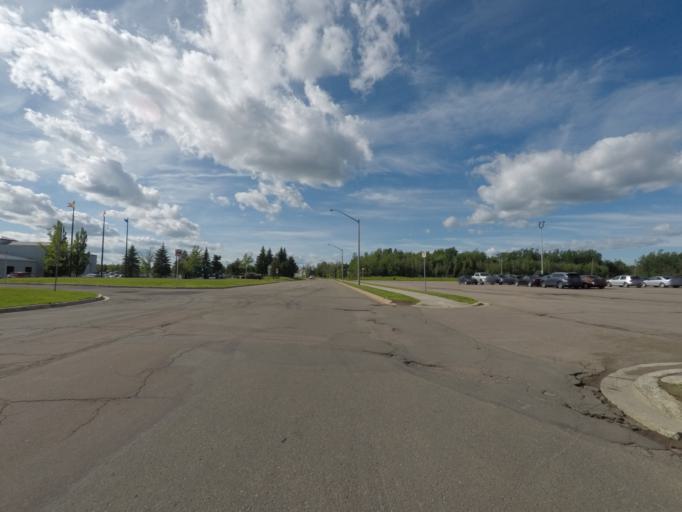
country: CA
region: New Brunswick
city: Moncton
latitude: 46.0958
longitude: -64.8329
